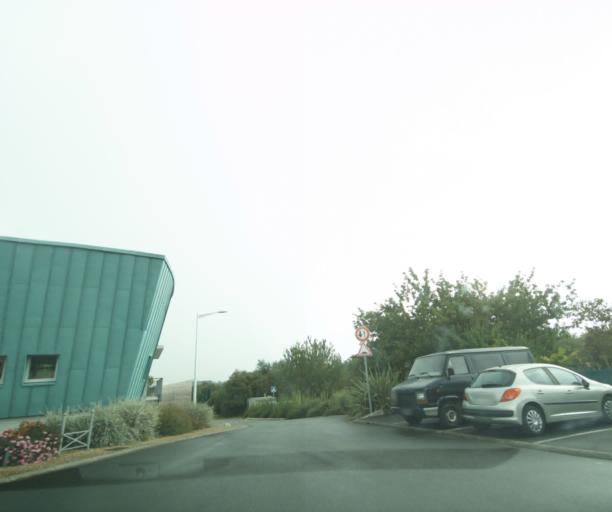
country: FR
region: Poitou-Charentes
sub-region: Departement de la Charente-Maritime
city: Tonnay-Charente
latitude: 45.9480
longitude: -0.8795
